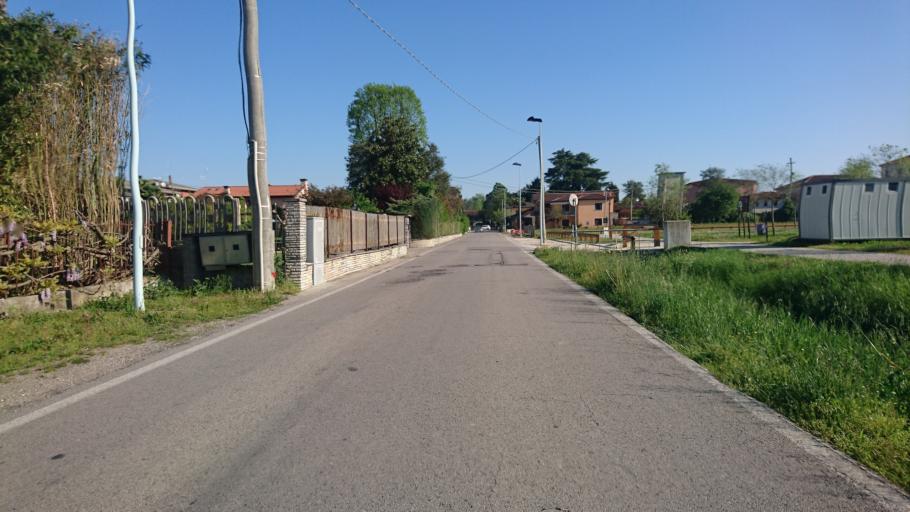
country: IT
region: Veneto
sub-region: Provincia di Padova
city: Massanzago-Ca' Baglioni-San Dono
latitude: 45.5538
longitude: 12.0029
